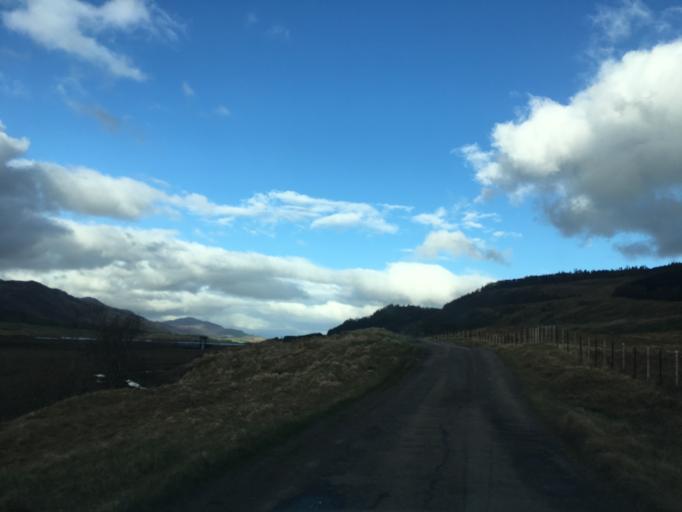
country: GB
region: Scotland
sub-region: Highland
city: Kingussie
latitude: 57.0056
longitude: -4.3760
